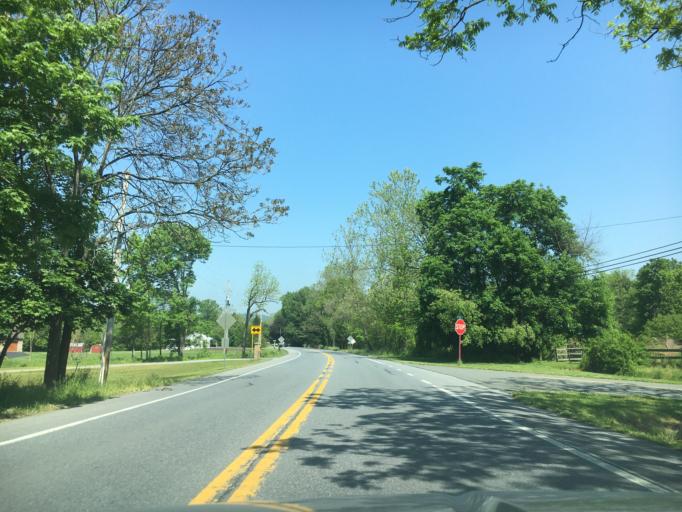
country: US
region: Pennsylvania
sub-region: Berks County
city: Oley
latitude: 40.3792
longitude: -75.7240
